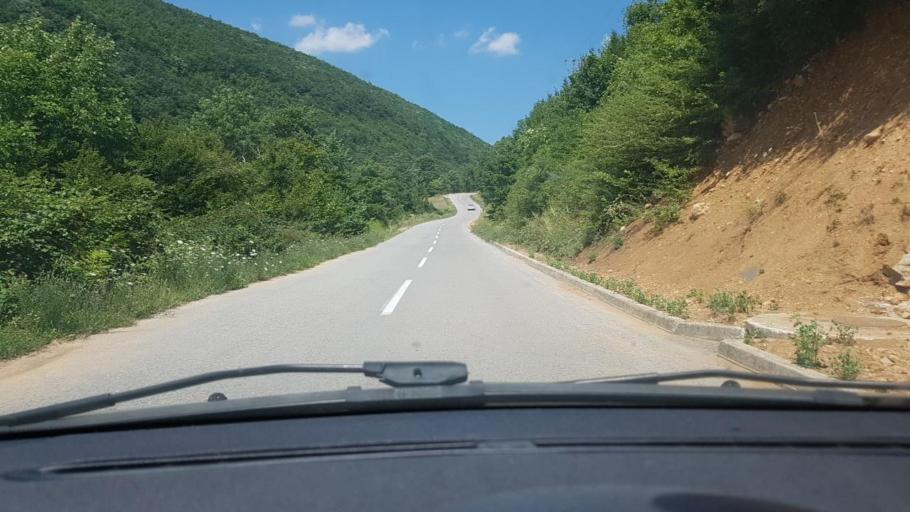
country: BA
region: Federation of Bosnia and Herzegovina
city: Orasac
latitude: 44.4985
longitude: 16.1331
